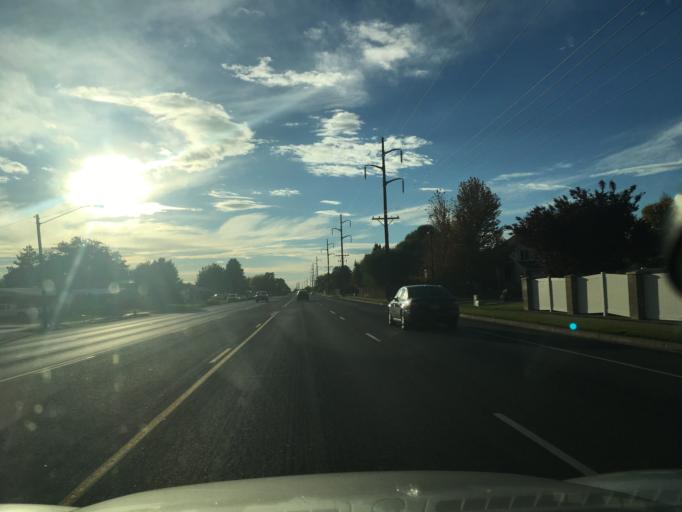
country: US
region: Utah
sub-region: Davis County
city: Layton
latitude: 41.0747
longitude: -111.9621
